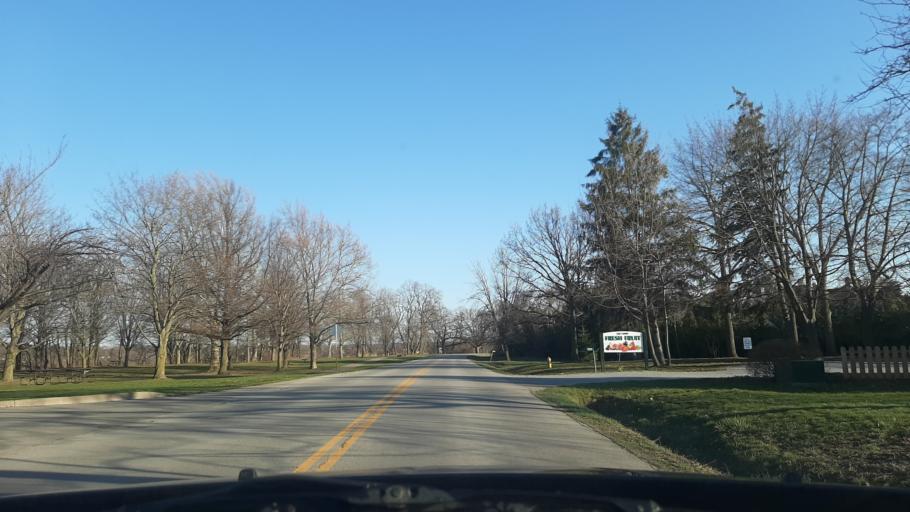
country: US
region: New York
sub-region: Niagara County
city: Youngstown
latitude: 43.2309
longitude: -79.0609
